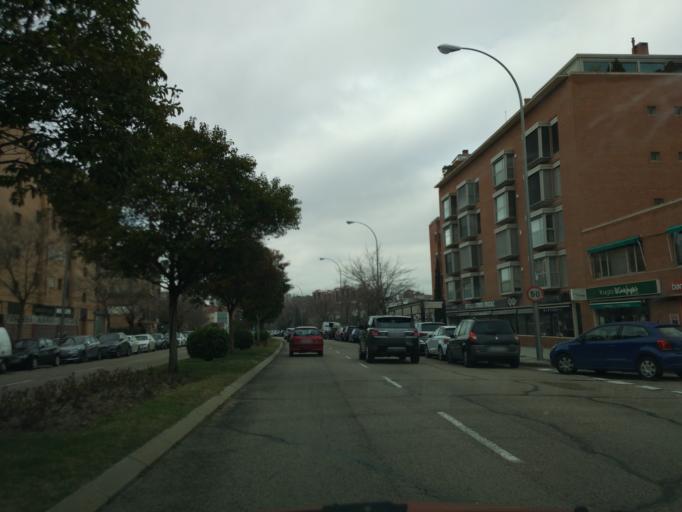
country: ES
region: Madrid
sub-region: Provincia de Madrid
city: Hortaleza
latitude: 40.4587
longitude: -3.6258
